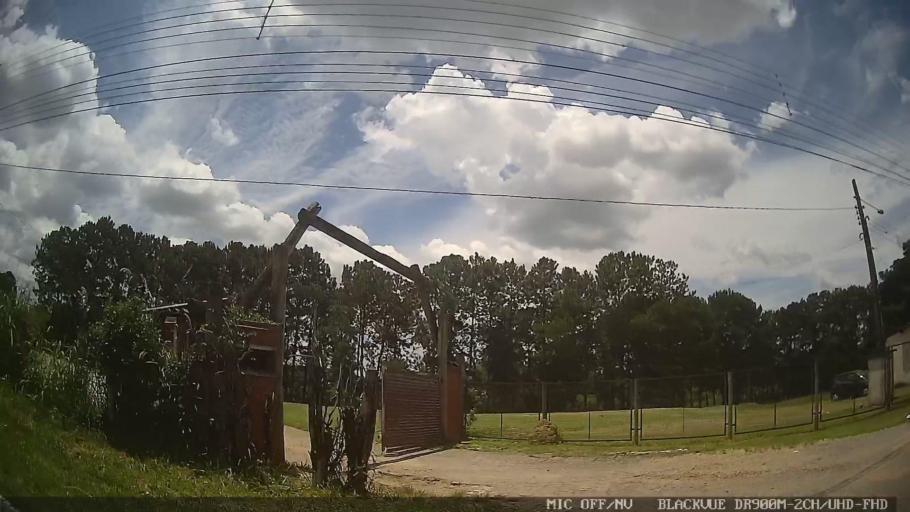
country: BR
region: Sao Paulo
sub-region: Atibaia
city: Atibaia
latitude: -23.1164
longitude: -46.5789
